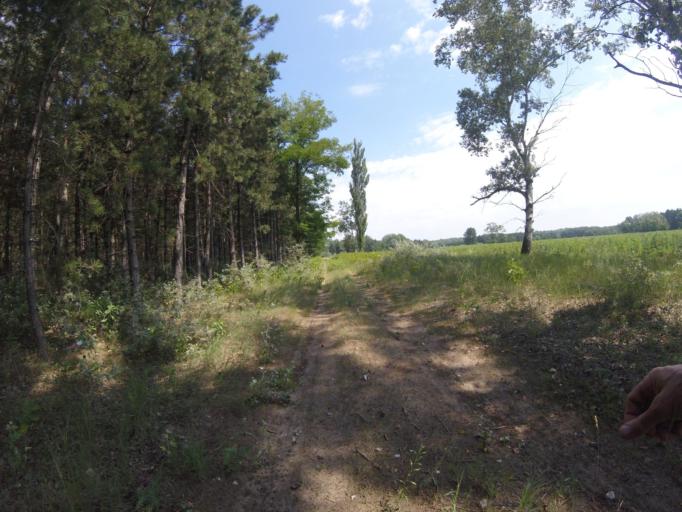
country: HU
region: Bacs-Kiskun
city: Jaszszentlaszlo
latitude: 46.6143
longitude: 19.7238
